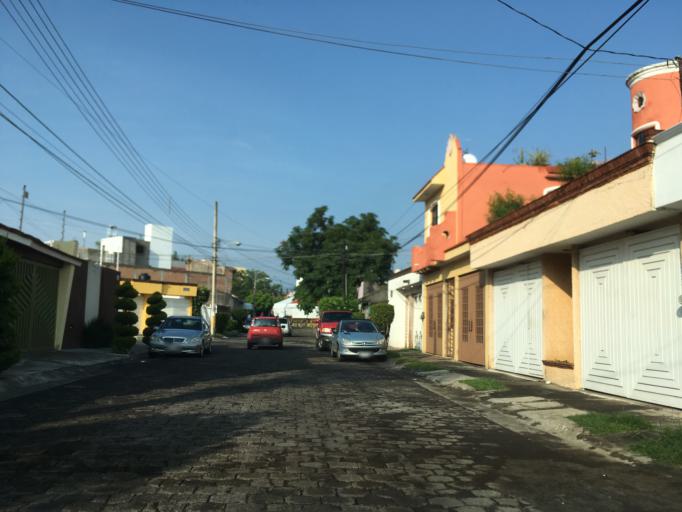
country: MX
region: Michoacan
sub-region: Morelia
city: Morelos
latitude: 19.6821
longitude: -101.2250
